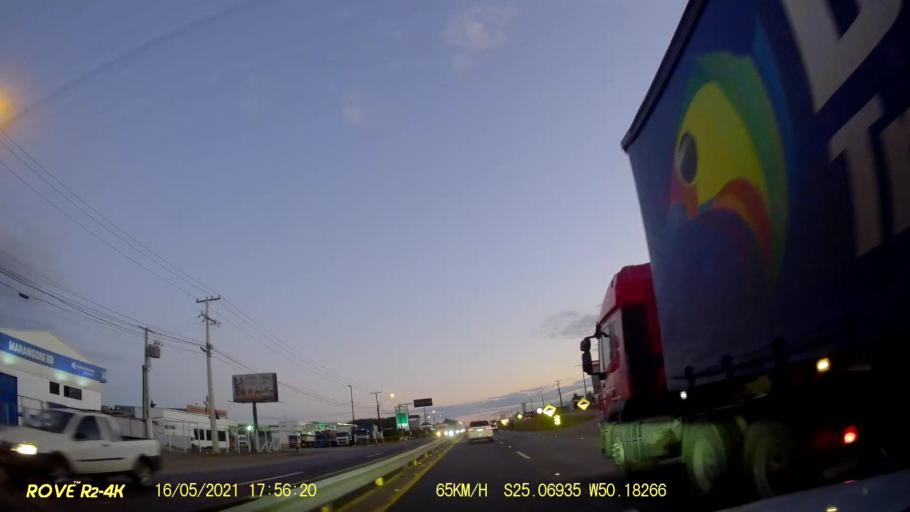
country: BR
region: Parana
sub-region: Ponta Grossa
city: Ponta Grossa
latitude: -25.0694
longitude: -50.1827
